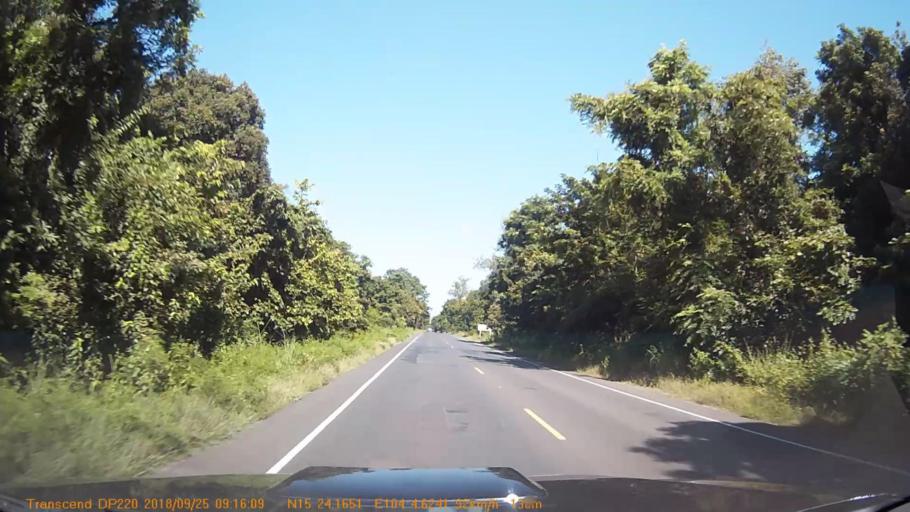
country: TH
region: Sisaket
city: Sila Lat
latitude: 15.4026
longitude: 104.0773
